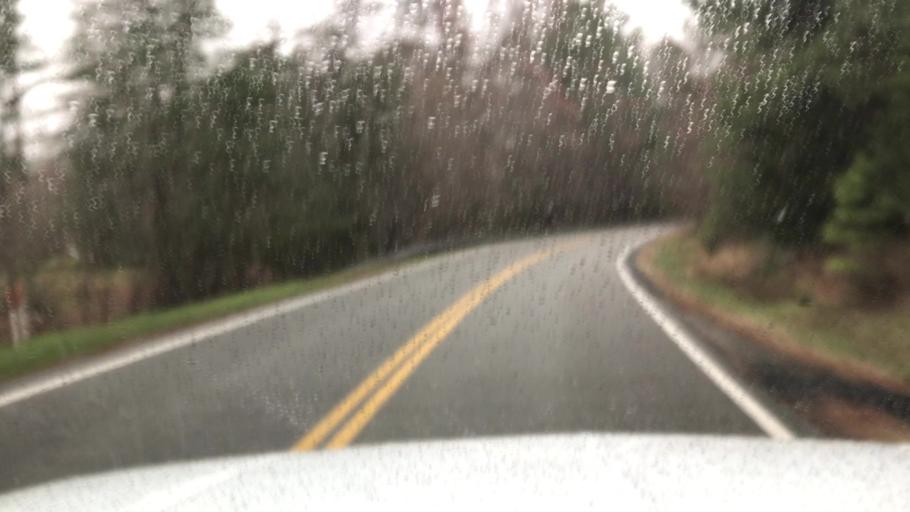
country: US
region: Virginia
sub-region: Henrico County
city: Short Pump
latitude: 37.6327
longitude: -77.6803
